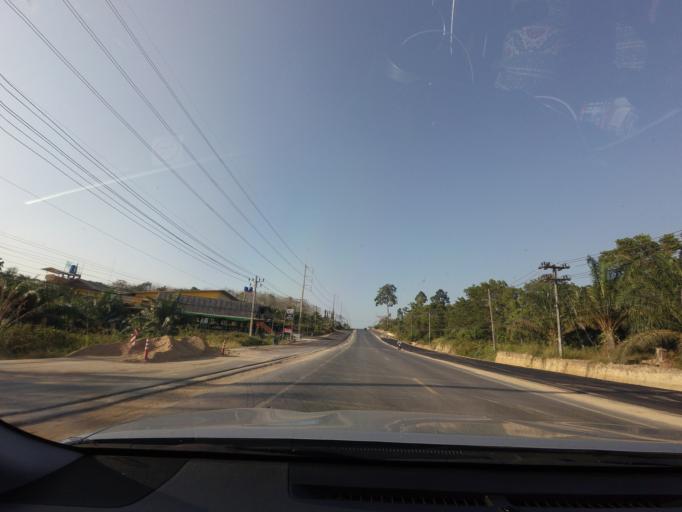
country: TH
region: Phangnga
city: Ban Khao Lak
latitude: 8.7192
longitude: 98.2567
